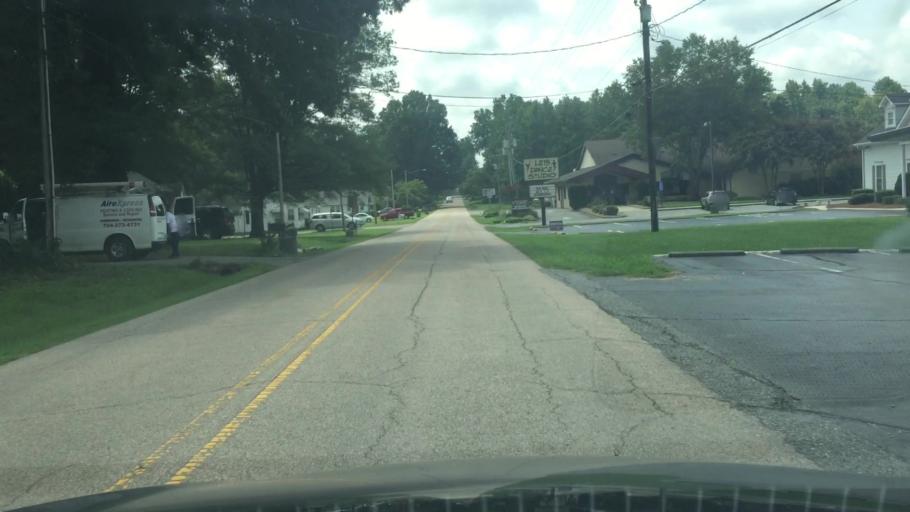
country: US
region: North Carolina
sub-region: Cabarrus County
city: Kannapolis
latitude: 35.4666
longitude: -80.6200
